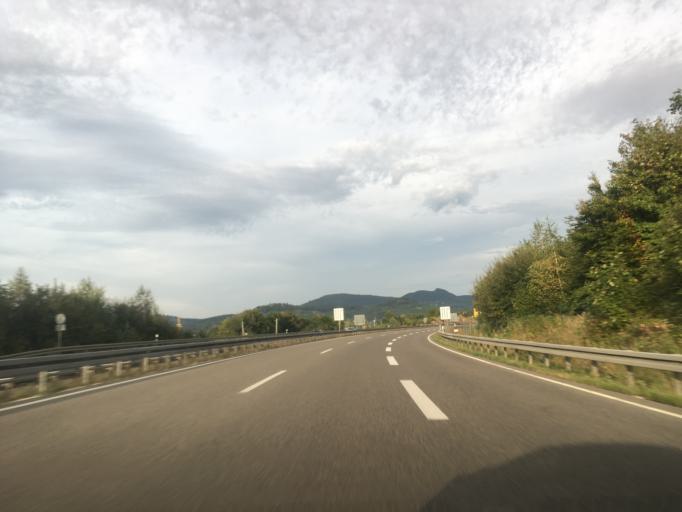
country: DE
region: Baden-Wuerttemberg
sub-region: Tuebingen Region
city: Metzingen
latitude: 48.5286
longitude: 9.2657
